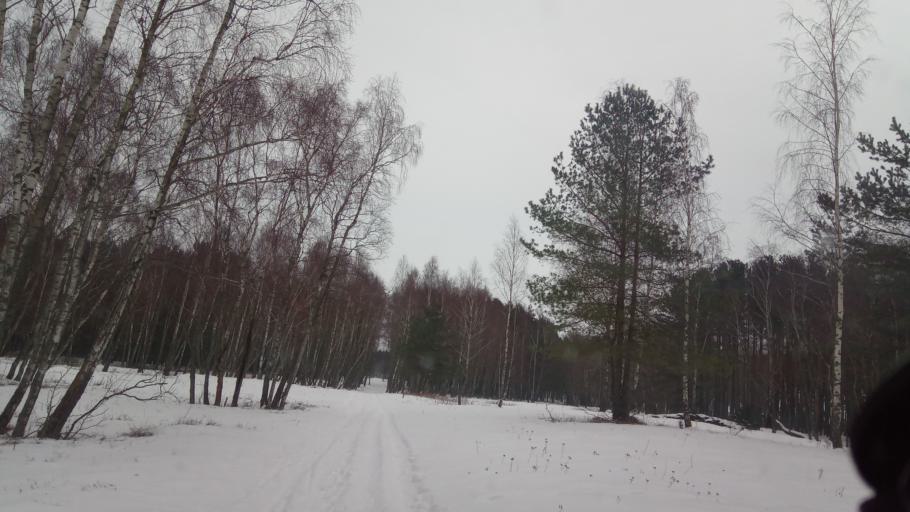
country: LT
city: Neringa
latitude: 55.4184
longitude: 21.1032
